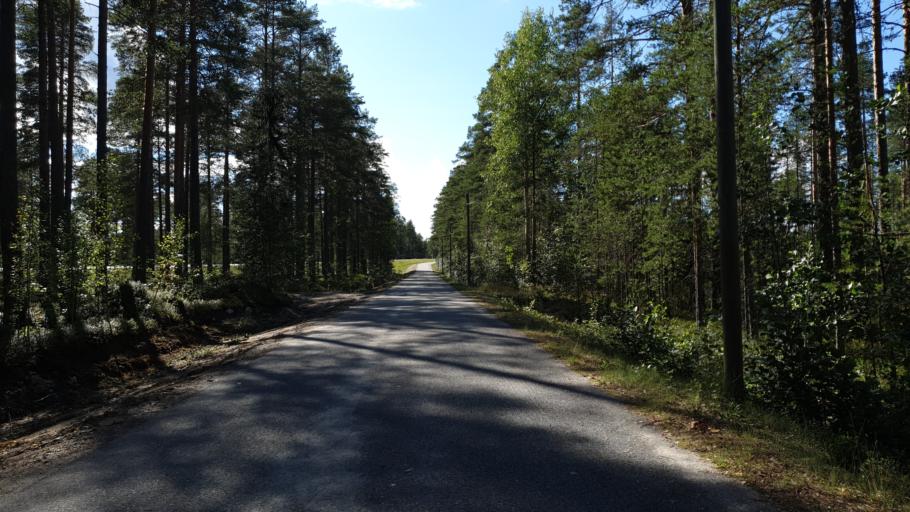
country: FI
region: Kainuu
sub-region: Kehys-Kainuu
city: Kuhmo
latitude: 64.0927
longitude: 29.4528
